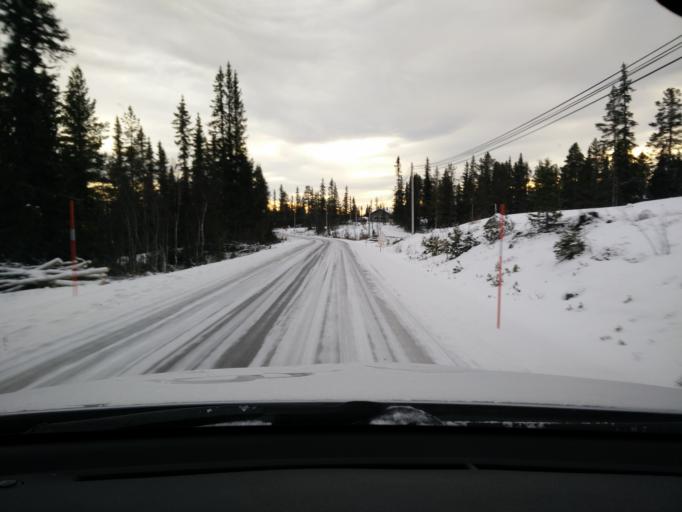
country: SE
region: Jaemtland
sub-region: Bergs Kommun
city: Hoverberg
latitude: 62.4815
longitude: 14.1227
